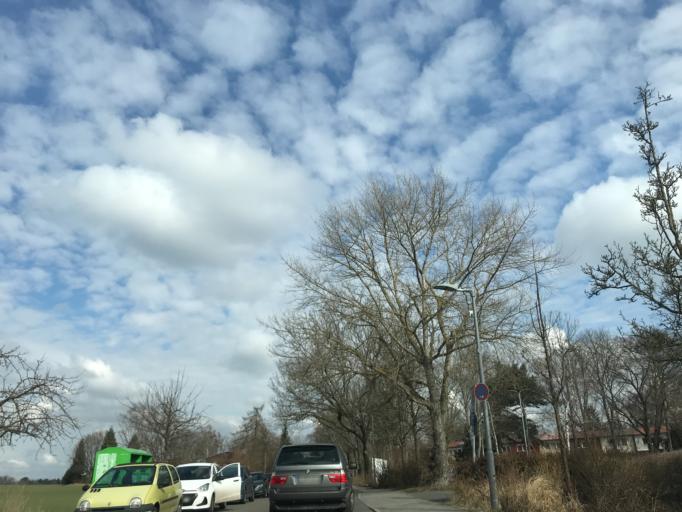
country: DE
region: Berlin
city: Kladow
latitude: 52.4551
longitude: 13.1436
